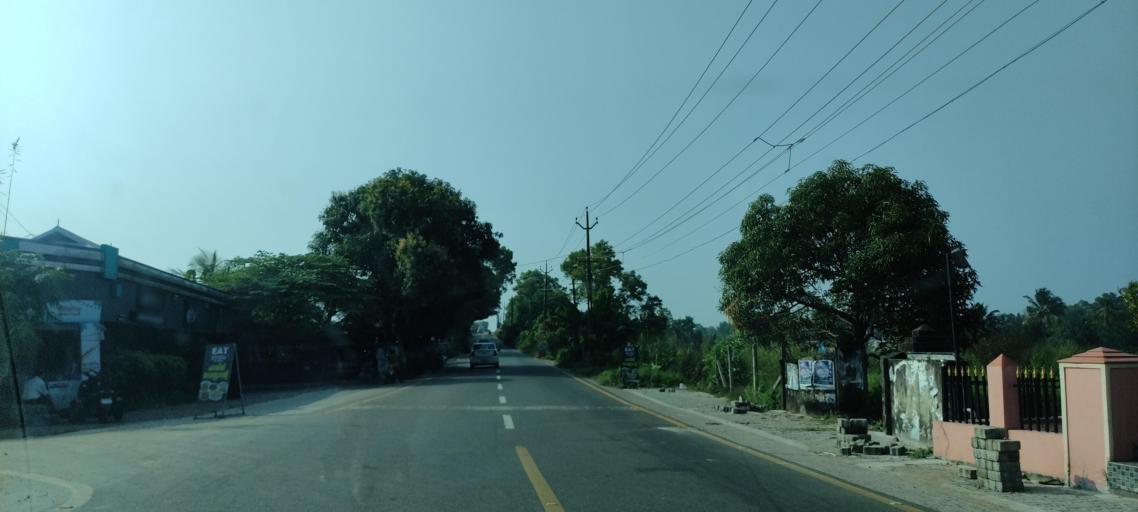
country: IN
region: Kerala
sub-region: Kottayam
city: Changanacheri
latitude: 9.3692
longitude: 76.4274
